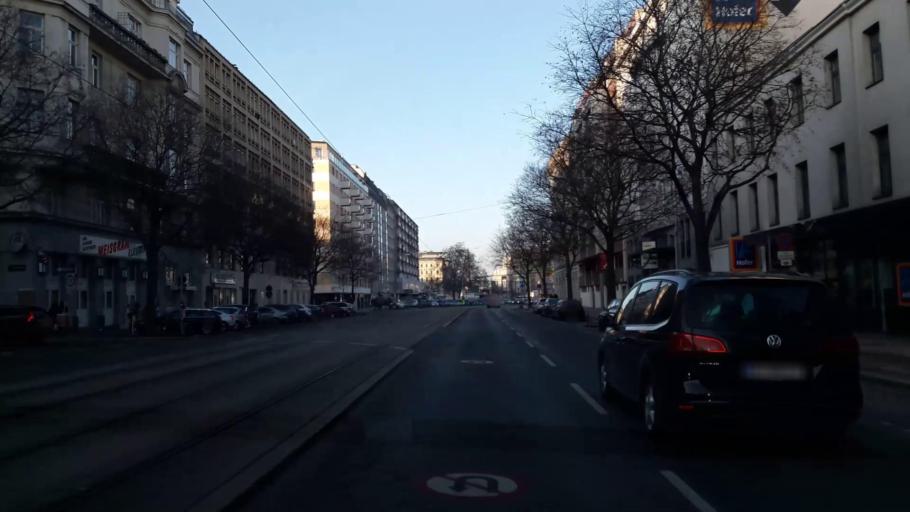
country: AT
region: Vienna
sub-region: Wien Stadt
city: Vienna
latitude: 48.2152
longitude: 16.3913
